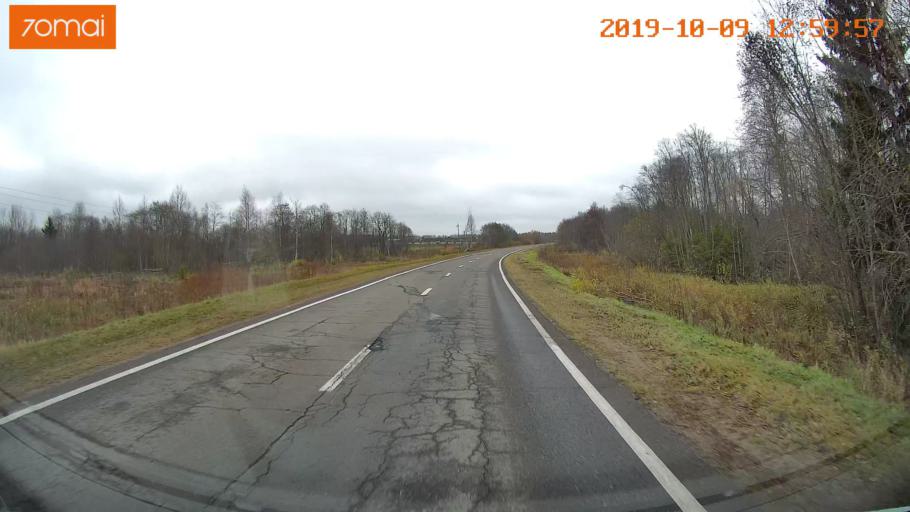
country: RU
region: Jaroslavl
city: Prechistoye
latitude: 58.3811
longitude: 40.4733
